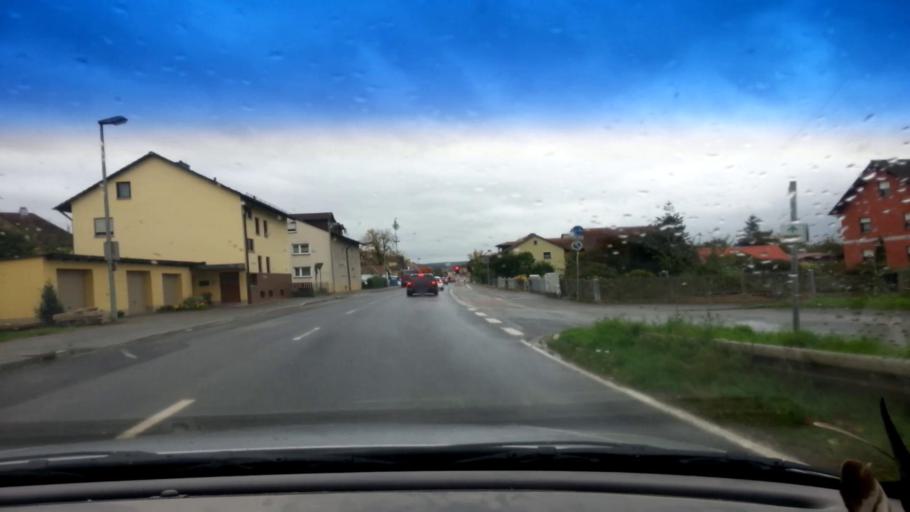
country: DE
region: Bavaria
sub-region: Upper Franconia
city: Viereth-Trunstadt
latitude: 49.9232
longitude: 10.7808
